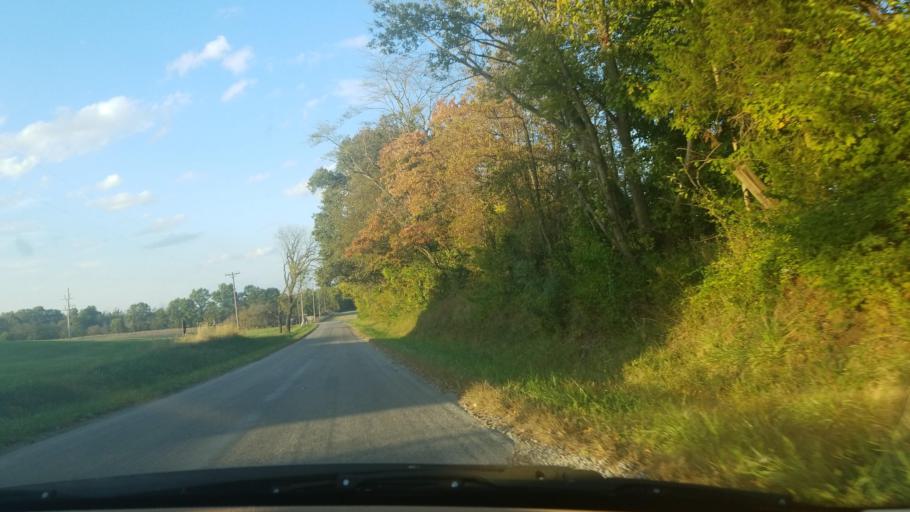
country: US
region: Illinois
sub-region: Saline County
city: Harrisburg
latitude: 37.8322
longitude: -88.6145
